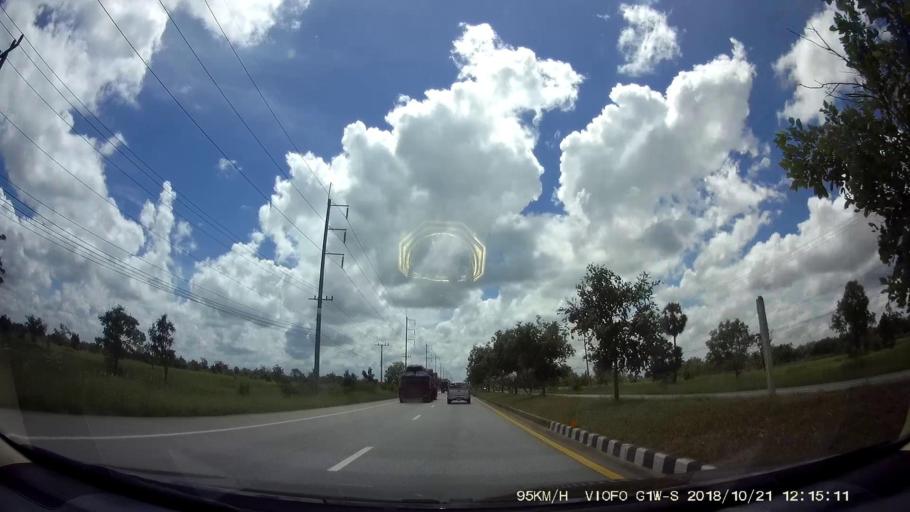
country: TH
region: Nakhon Ratchasima
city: Dan Khun Thot
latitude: 15.3662
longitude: 101.8316
